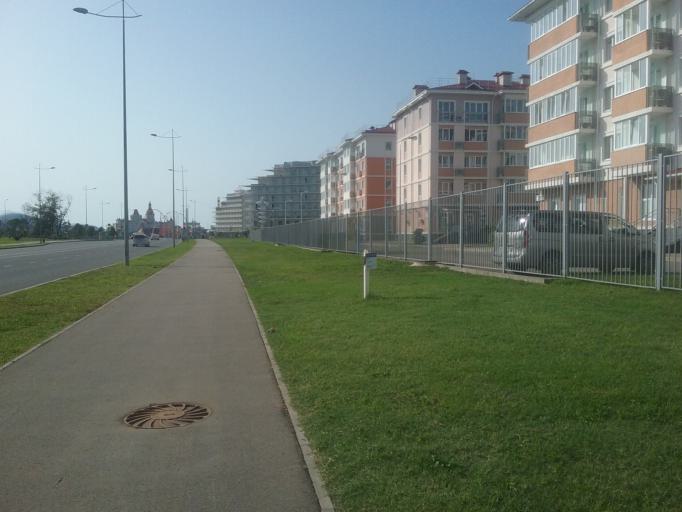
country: RU
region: Krasnodarskiy
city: Adler
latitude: 43.4000
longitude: 39.9794
